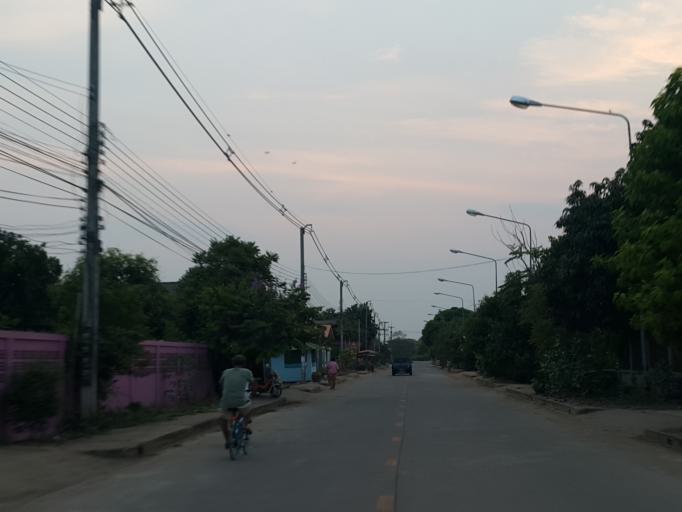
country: TH
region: Sukhothai
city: Sawankhalok
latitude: 17.3109
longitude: 99.8185
